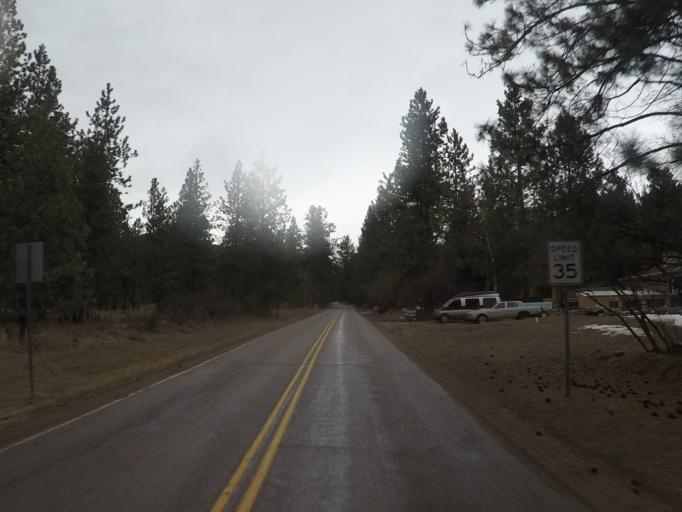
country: US
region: Montana
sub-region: Missoula County
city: East Missoula
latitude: 46.9096
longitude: -113.9604
